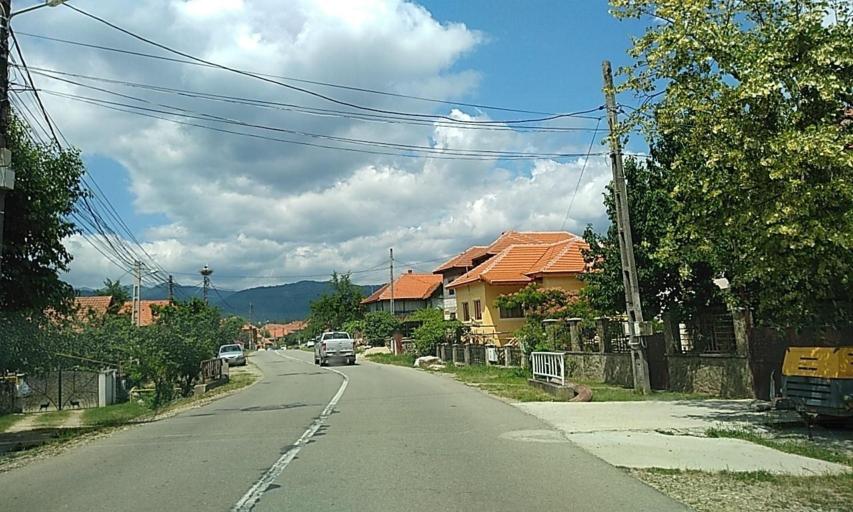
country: RO
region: Gorj
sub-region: Comuna Bumbesti-Jiu
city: Bumbesti-Jiu
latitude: 45.1511
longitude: 23.3934
